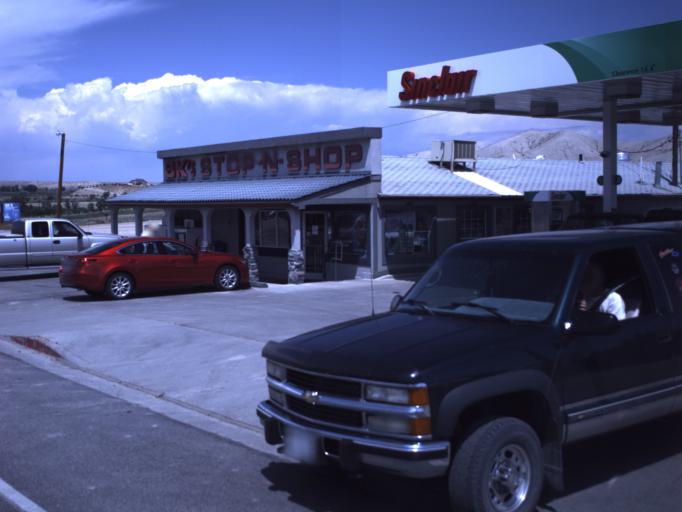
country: US
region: Utah
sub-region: Emery County
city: Huntington
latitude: 39.3348
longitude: -110.9646
